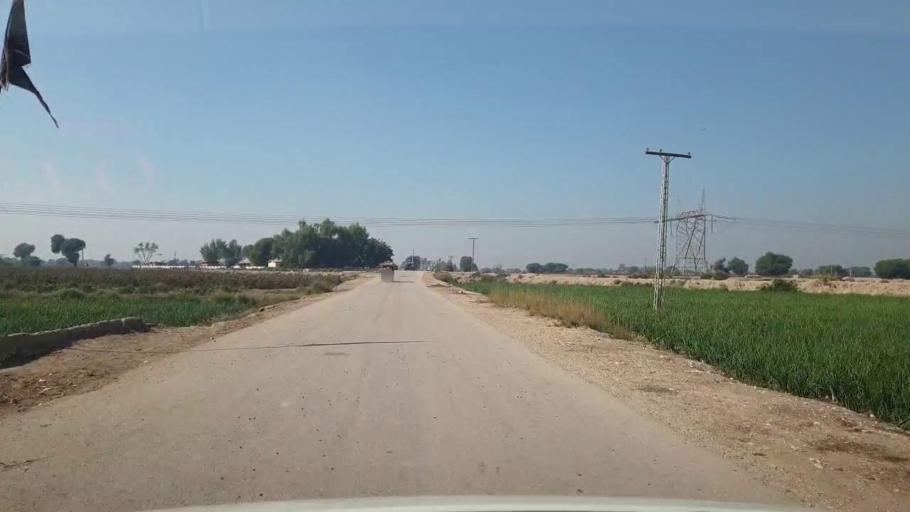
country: PK
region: Sindh
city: Bhan
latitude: 26.6457
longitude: 67.7269
